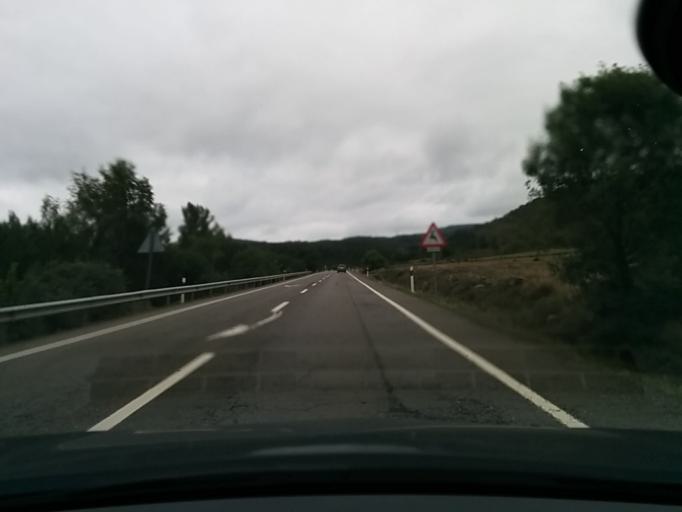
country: ES
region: Aragon
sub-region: Provincia de Huesca
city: Sabinanigo
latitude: 42.4440
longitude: -0.3933
